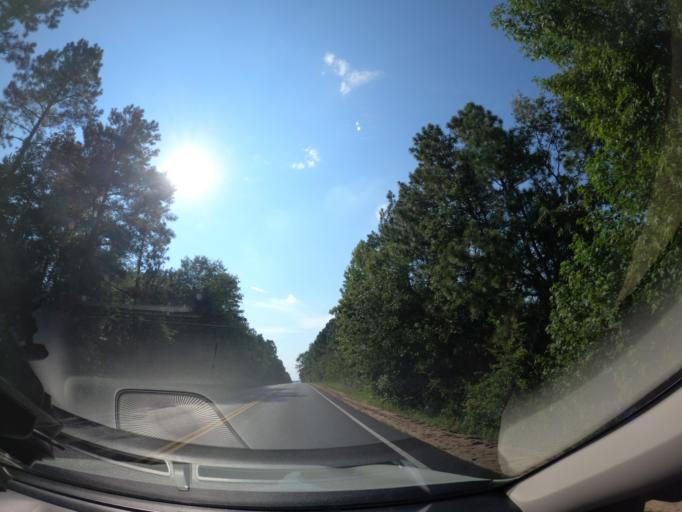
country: US
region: South Carolina
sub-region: Aiken County
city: Jackson
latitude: 33.4032
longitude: -81.7712
